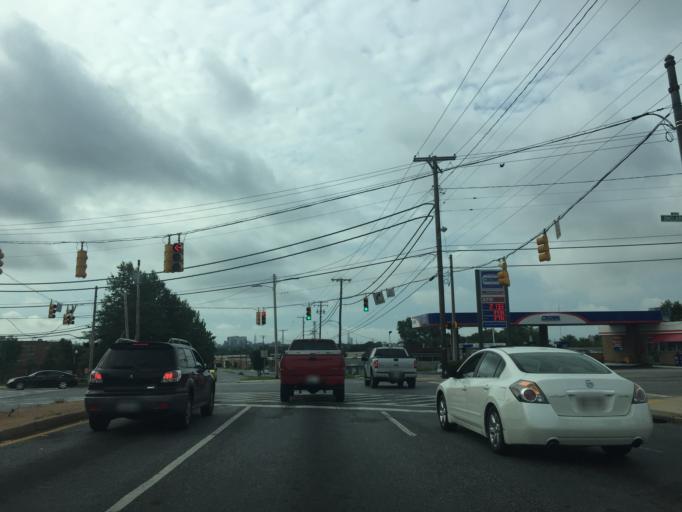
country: US
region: Maryland
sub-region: City of Baltimore
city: Baltimore
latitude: 39.3138
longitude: -76.5679
